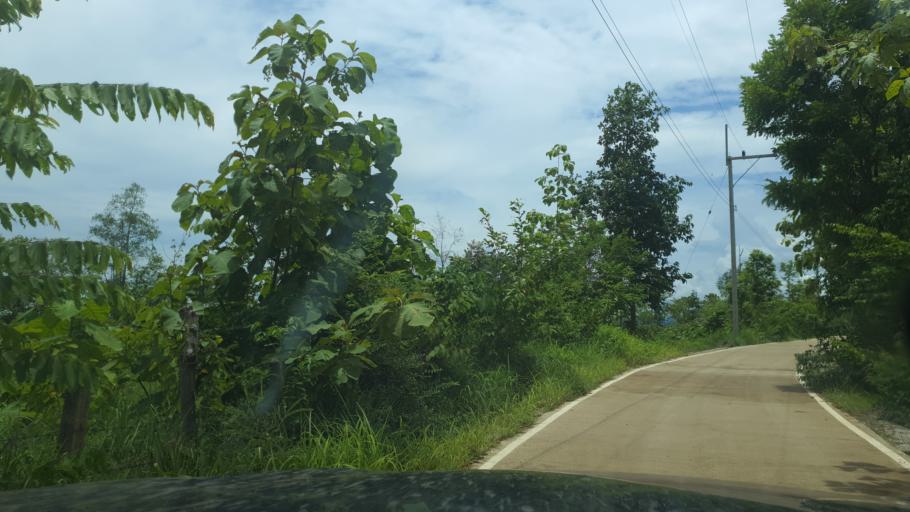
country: TH
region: Lampang
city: Ko Kha
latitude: 18.1366
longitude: 99.3287
